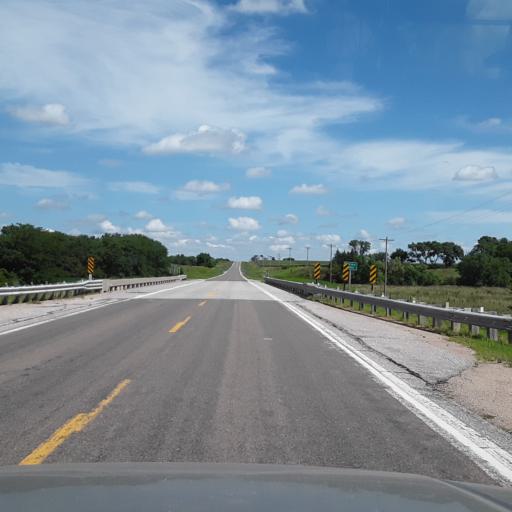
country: US
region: Nebraska
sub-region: York County
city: York
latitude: 40.9827
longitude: -97.4063
